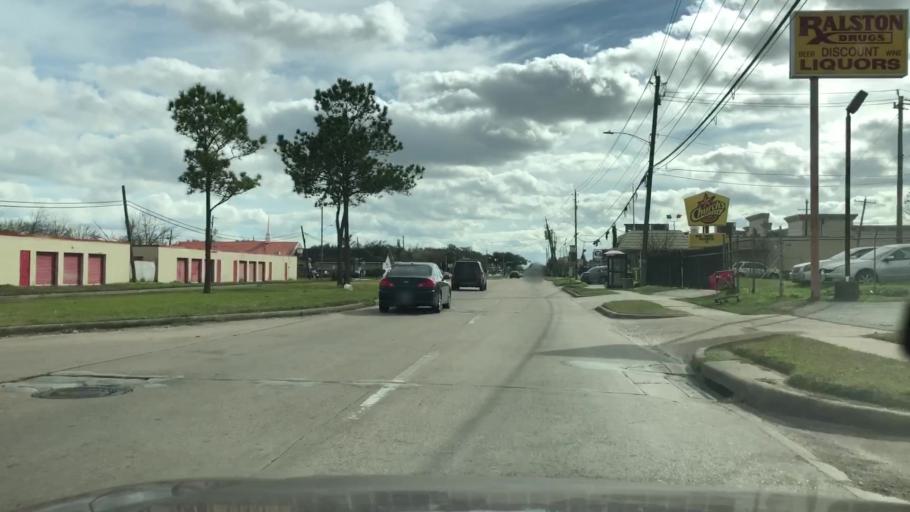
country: US
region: Texas
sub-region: Fort Bend County
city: Missouri City
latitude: 29.6175
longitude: -95.4651
